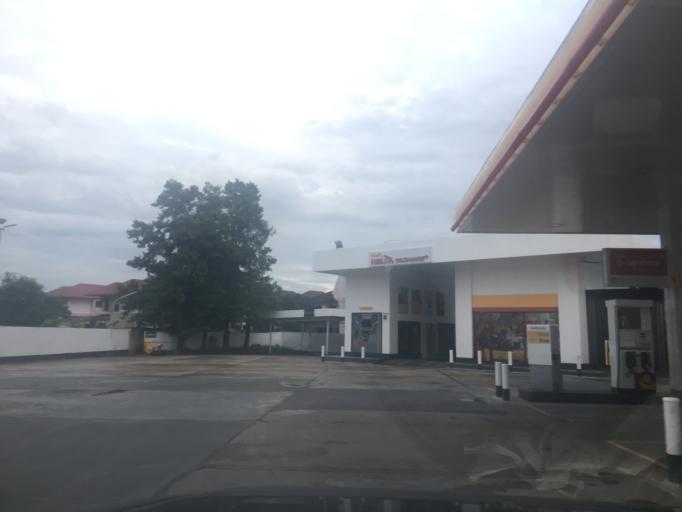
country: TH
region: Chiang Mai
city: San Sai
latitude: 18.8178
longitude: 99.0368
